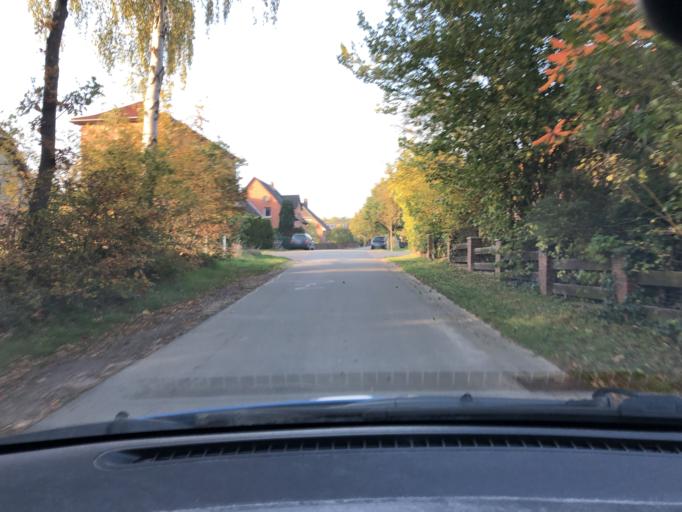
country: DE
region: Lower Saxony
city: Hitzacker
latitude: 53.1502
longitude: 11.0040
